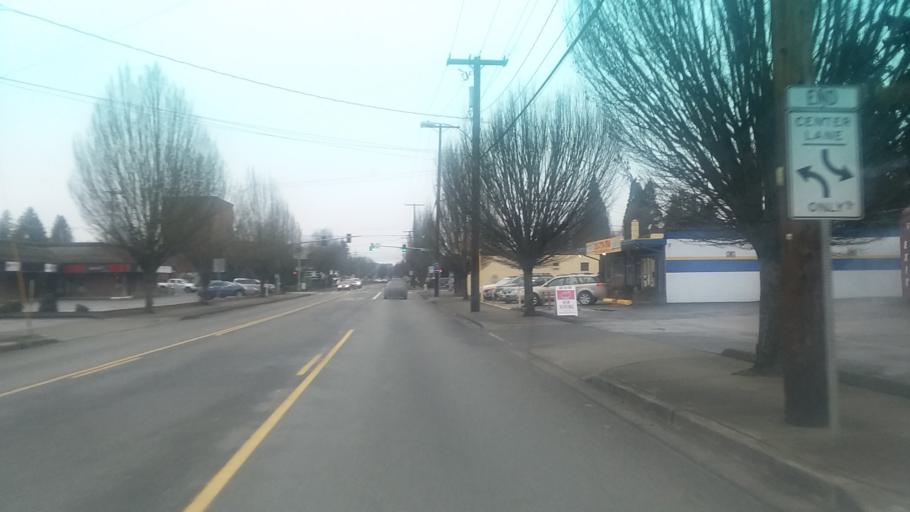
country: US
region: Washington
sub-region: Pierce County
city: Puyallup
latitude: 47.1919
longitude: -122.2865
